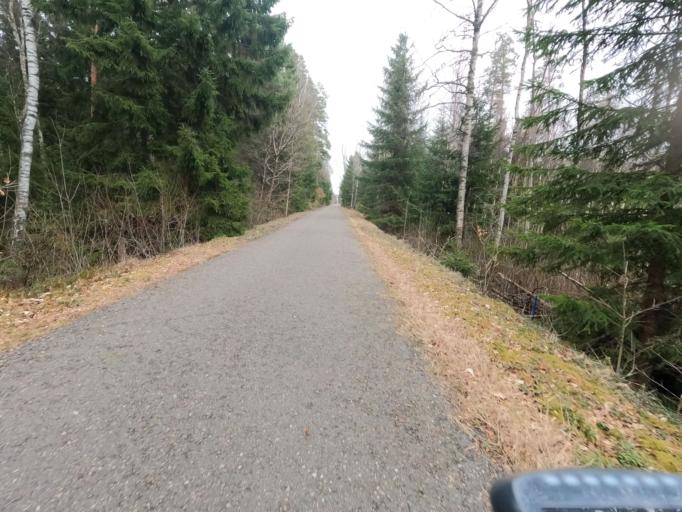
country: SE
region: Joenkoeping
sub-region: Varnamo Kommun
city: Rydaholm
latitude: 56.8472
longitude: 14.2111
